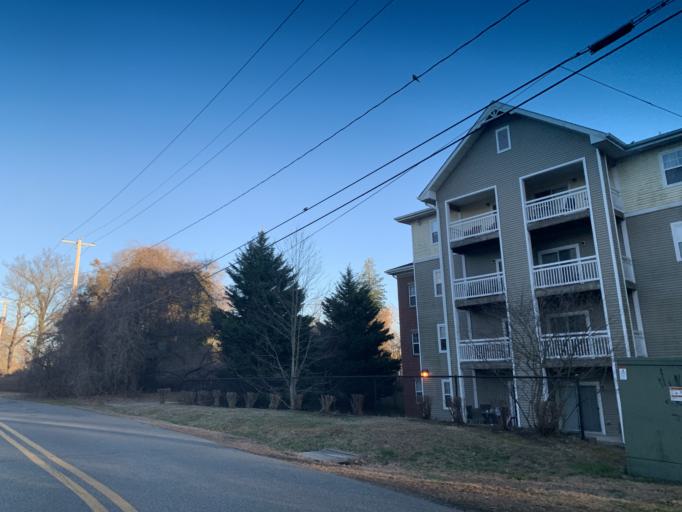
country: US
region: Maryland
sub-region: Cecil County
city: Perryville
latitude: 39.5646
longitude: -76.0735
